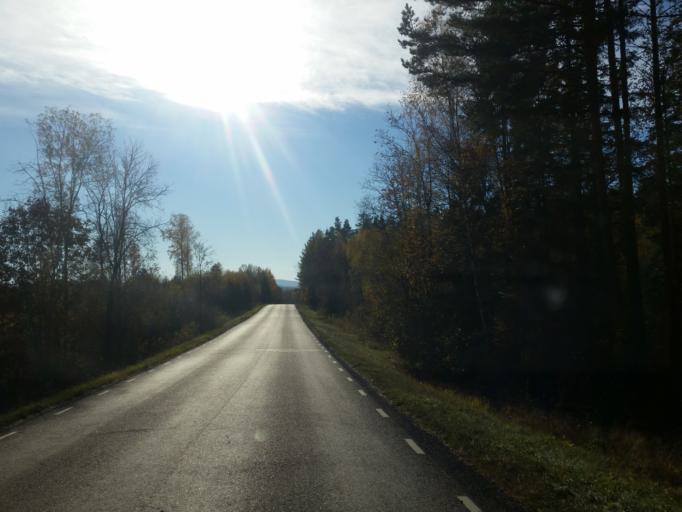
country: SE
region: Dalarna
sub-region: Borlange Kommun
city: Ornas
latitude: 60.5115
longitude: 15.5230
